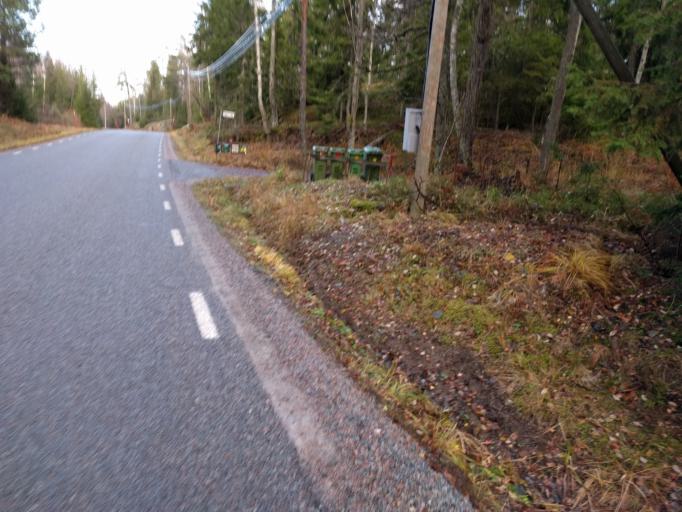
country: SE
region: Stockholm
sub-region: Osterakers Kommun
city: Akersberga
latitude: 59.6024
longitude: 18.3612
